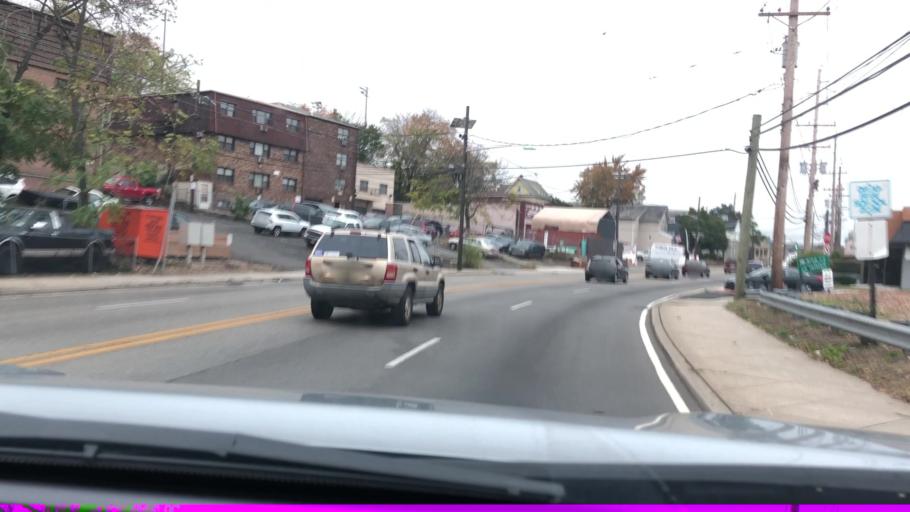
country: US
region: New Jersey
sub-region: Bergen County
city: Ridgefield
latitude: 40.8241
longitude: -74.0087
